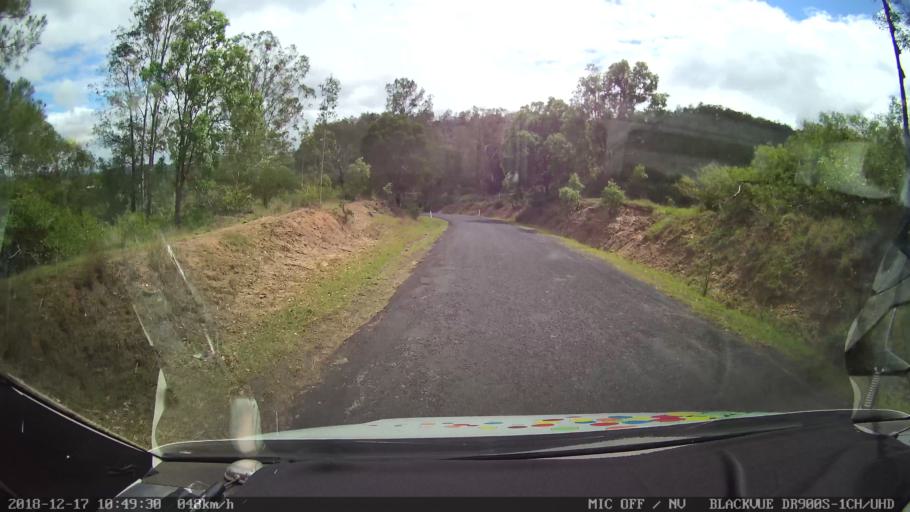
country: AU
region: New South Wales
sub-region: Clarence Valley
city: Gordon
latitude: -28.8653
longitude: 152.5735
